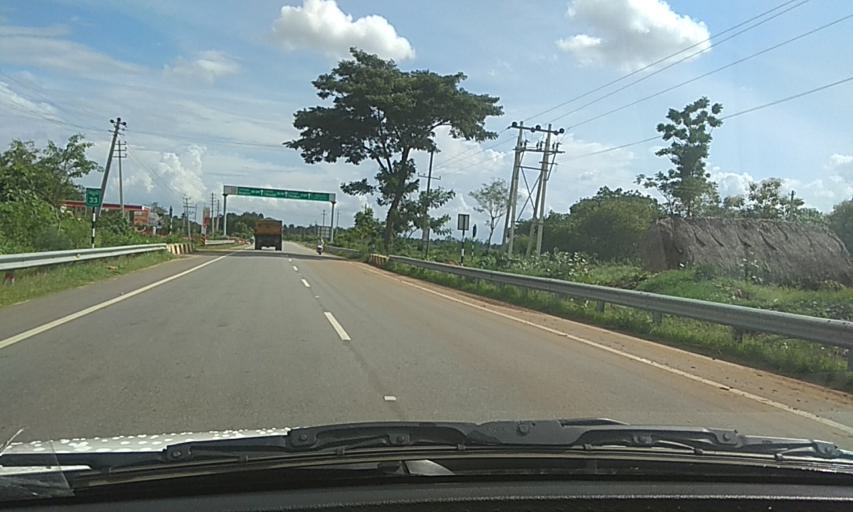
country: IN
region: Karnataka
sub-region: Mandya
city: Maddur
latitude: 12.6581
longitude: 77.0529
